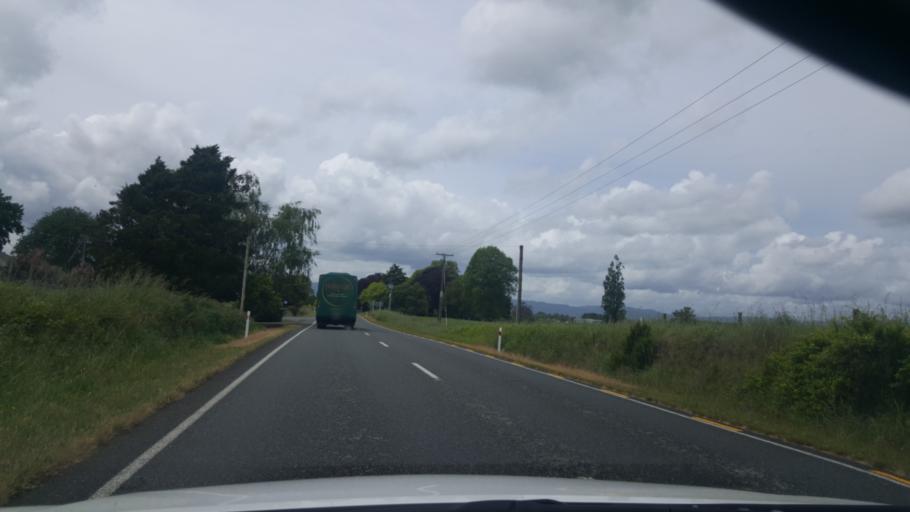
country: NZ
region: Waikato
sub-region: Matamata-Piako District
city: Matamata
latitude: -37.8762
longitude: 175.7205
